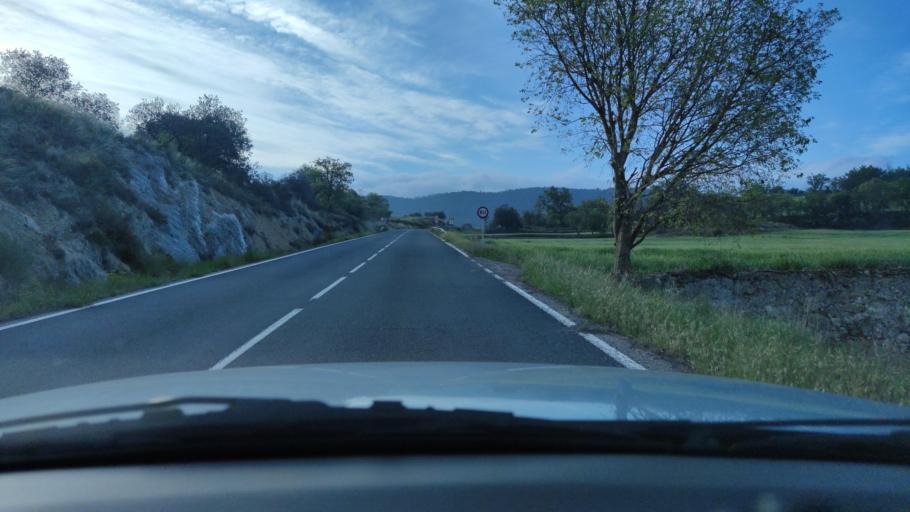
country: ES
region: Catalonia
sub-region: Provincia de Lleida
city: Ponts
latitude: 41.8928
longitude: 1.1775
